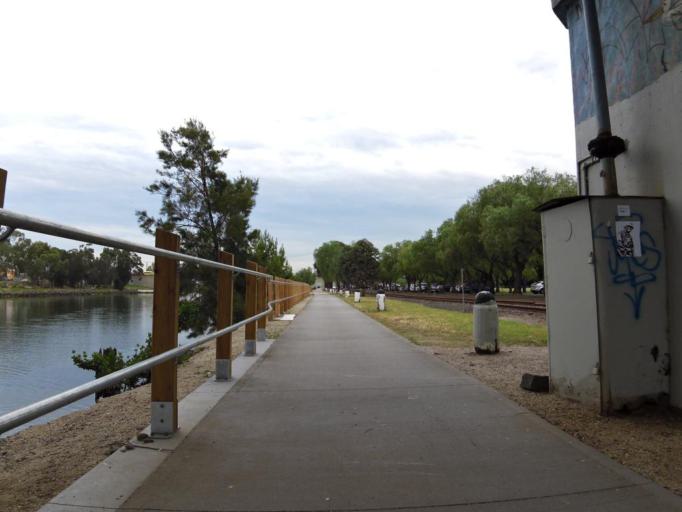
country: AU
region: Victoria
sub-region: Maribyrnong
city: Footscray
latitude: -37.8040
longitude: 144.9081
